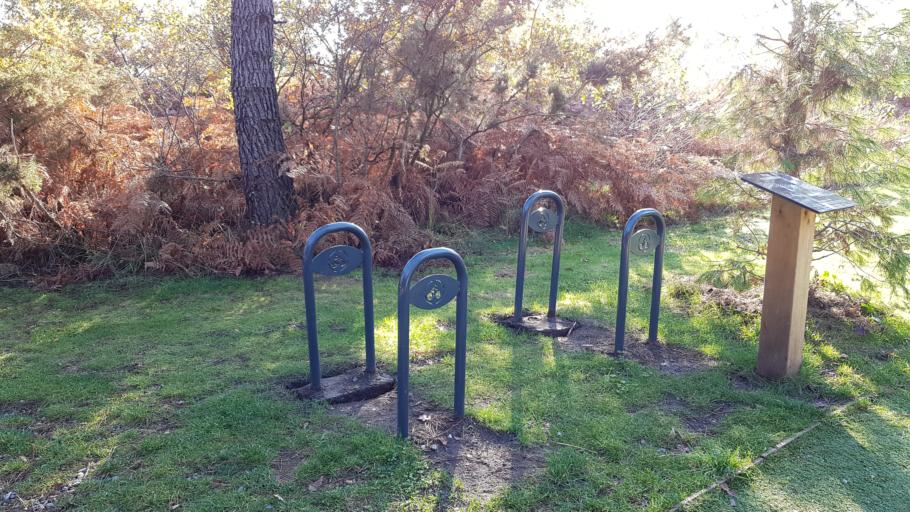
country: FR
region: Aquitaine
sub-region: Departement des Landes
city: Saint-Paul-les-Dax
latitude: 43.7360
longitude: -1.0850
